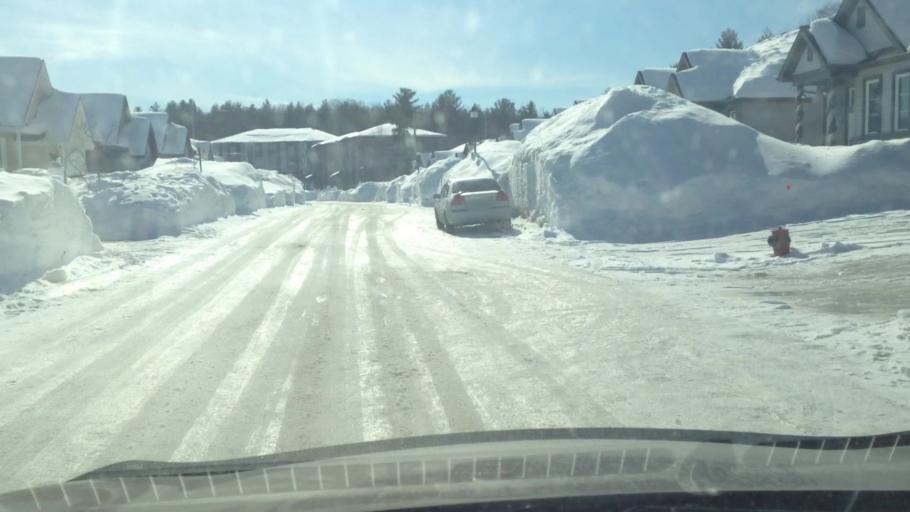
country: CA
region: Quebec
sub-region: Laurentides
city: Saint-Jerome
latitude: 45.7812
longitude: -73.9707
